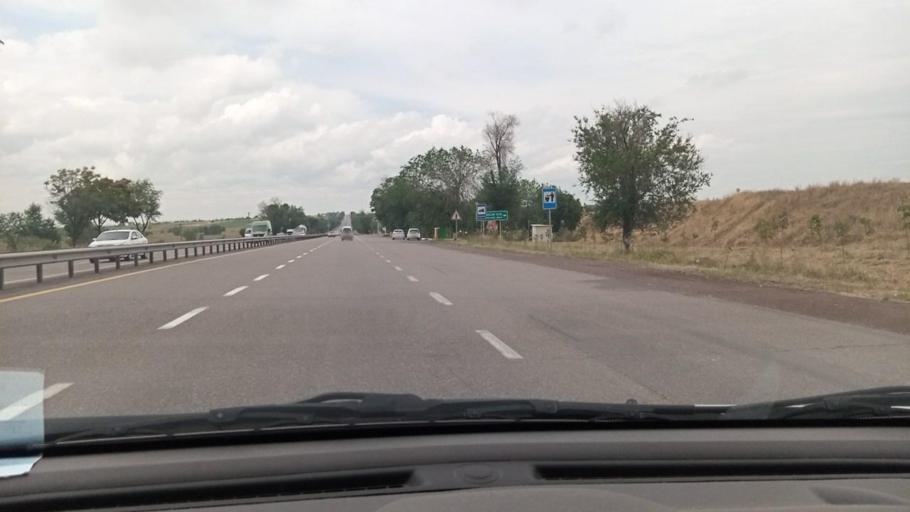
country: UZ
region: Toshkent
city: Ohangaron
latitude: 40.9940
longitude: 69.5312
